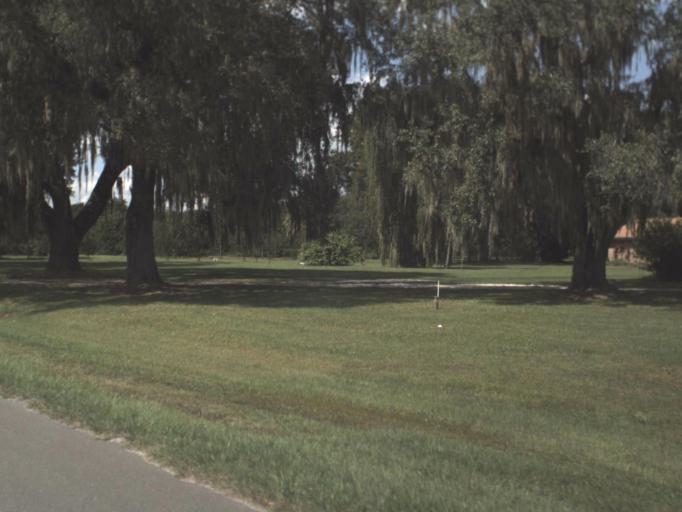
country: US
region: Florida
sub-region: Hardee County
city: Zolfo Springs
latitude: 27.4885
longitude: -81.7592
